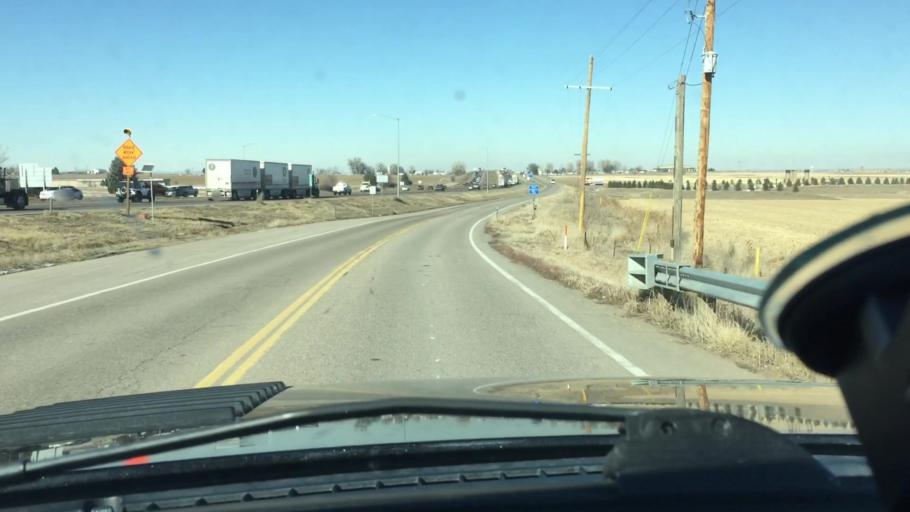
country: US
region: Colorado
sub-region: Weld County
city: Johnstown
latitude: 40.3381
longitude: -104.9797
